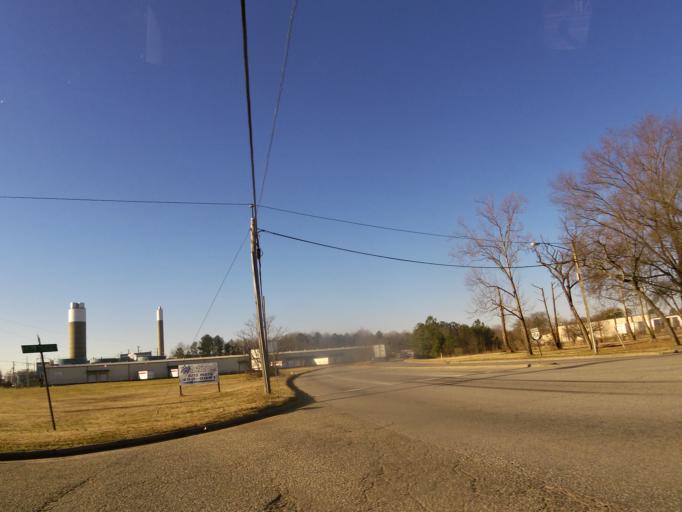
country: US
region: Virginia
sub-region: City of Hopewell
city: Hopewell
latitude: 37.2948
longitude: -77.2799
